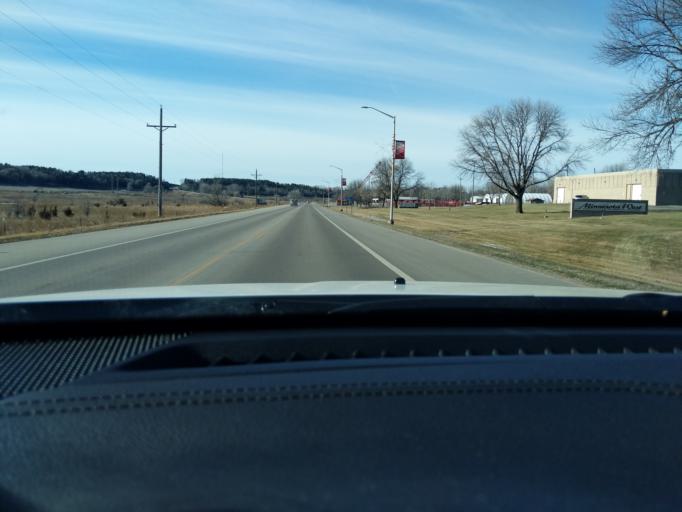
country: US
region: Minnesota
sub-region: Yellow Medicine County
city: Granite Falls
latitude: 44.8065
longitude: -95.5610
